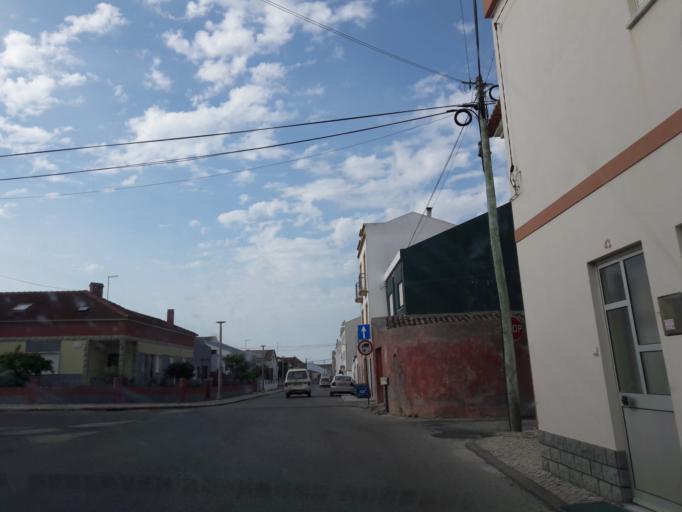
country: PT
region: Leiria
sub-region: Peniche
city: Atouguia da Baleia
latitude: 39.3378
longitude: -9.3274
